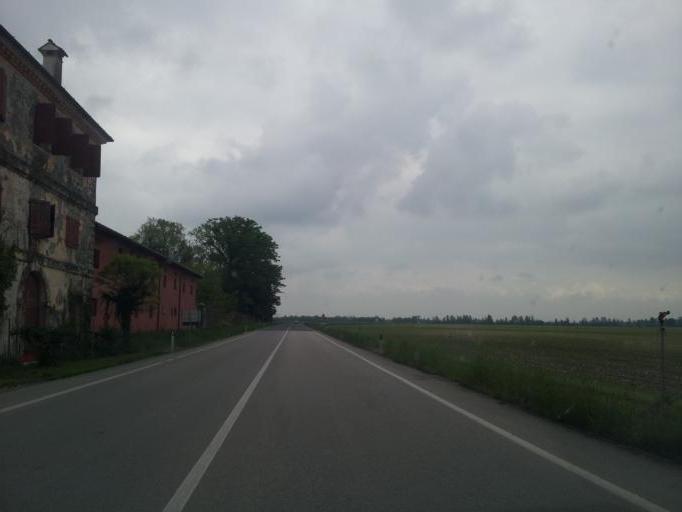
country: IT
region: Friuli Venezia Giulia
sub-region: Provincia di Udine
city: Varmo
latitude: 45.9201
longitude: 12.9929
